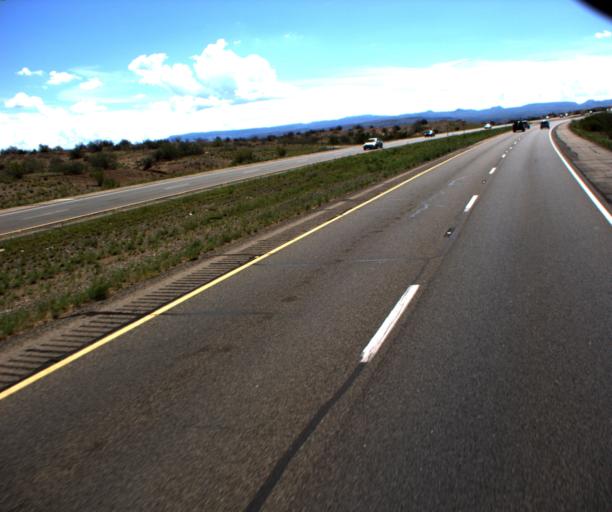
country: US
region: Arizona
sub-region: Yavapai County
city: Spring Valley
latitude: 34.3471
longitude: -112.1465
